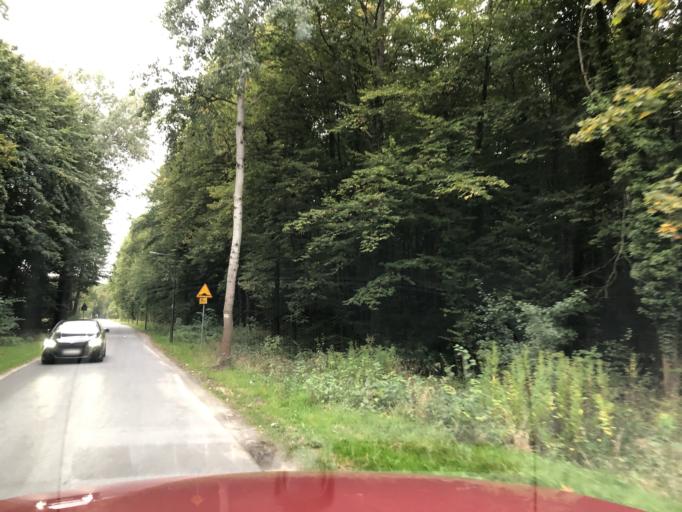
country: PL
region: Lower Silesian Voivodeship
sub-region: Powiat wroclawski
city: Dlugoleka
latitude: 51.1932
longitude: 17.1900
